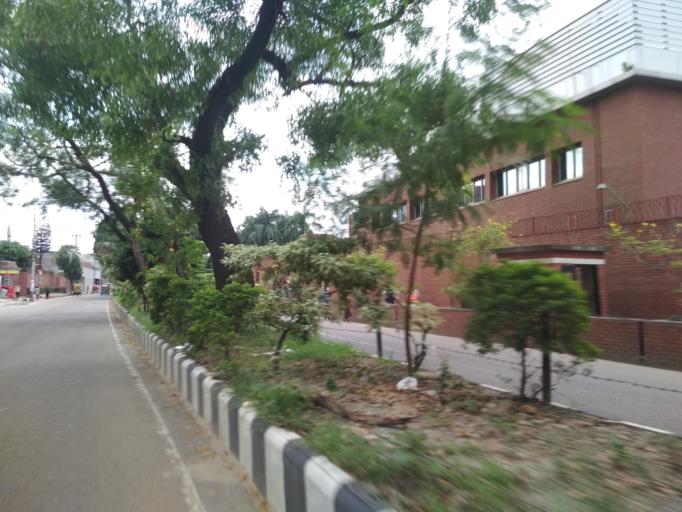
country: BD
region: Dhaka
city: Paltan
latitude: 23.7970
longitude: 90.4207
